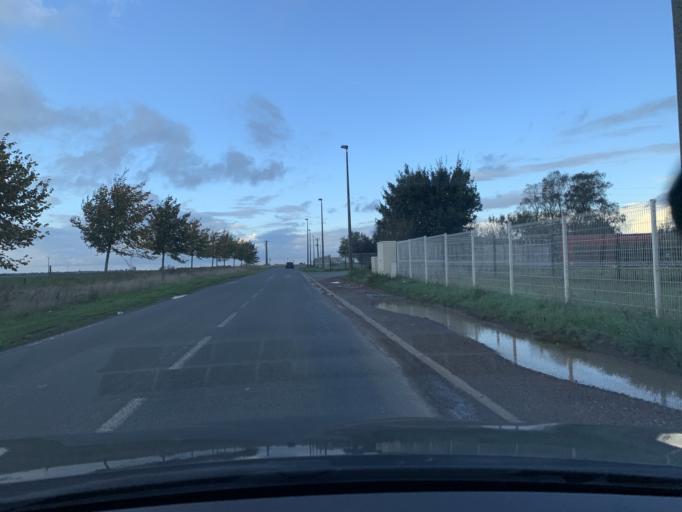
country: FR
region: Nord-Pas-de-Calais
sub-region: Departement du Nord
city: Proville
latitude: 50.1463
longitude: 3.2107
